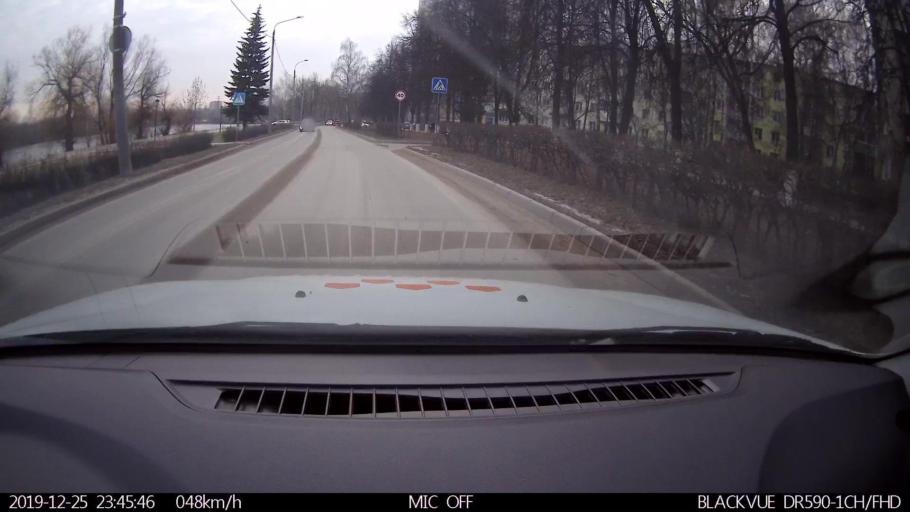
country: RU
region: Nizjnij Novgorod
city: Gorbatovka
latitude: 56.3420
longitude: 43.8482
